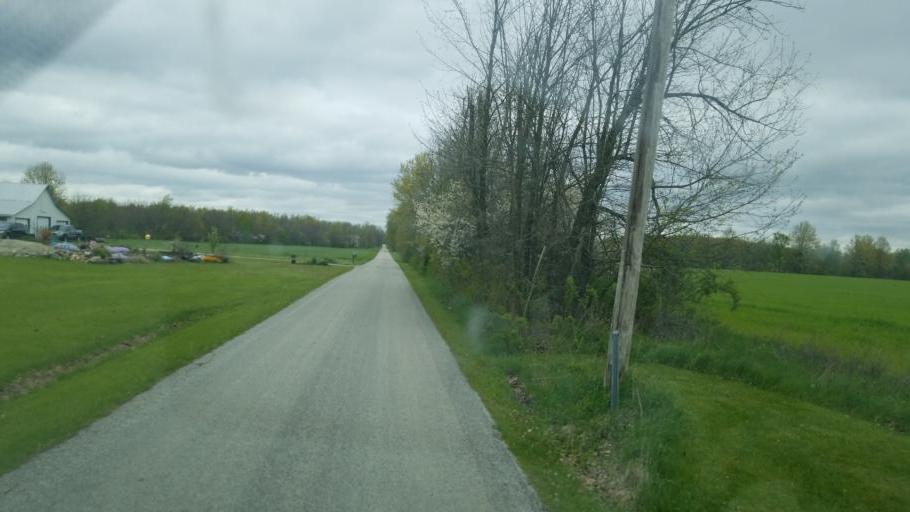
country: US
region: Ohio
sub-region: Marion County
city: Marion
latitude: 40.6234
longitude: -83.2790
